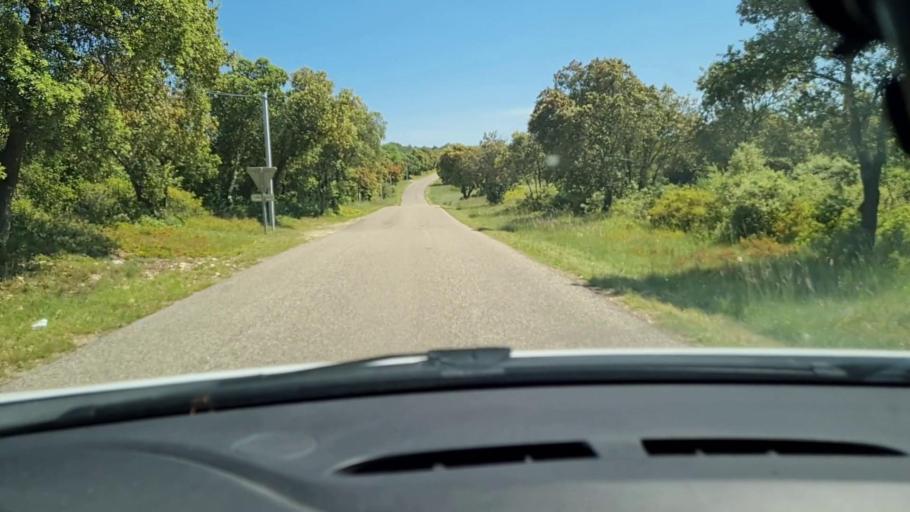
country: FR
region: Languedoc-Roussillon
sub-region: Departement du Gard
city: Saint-Mamert-du-Gard
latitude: 43.8561
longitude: 4.1885
